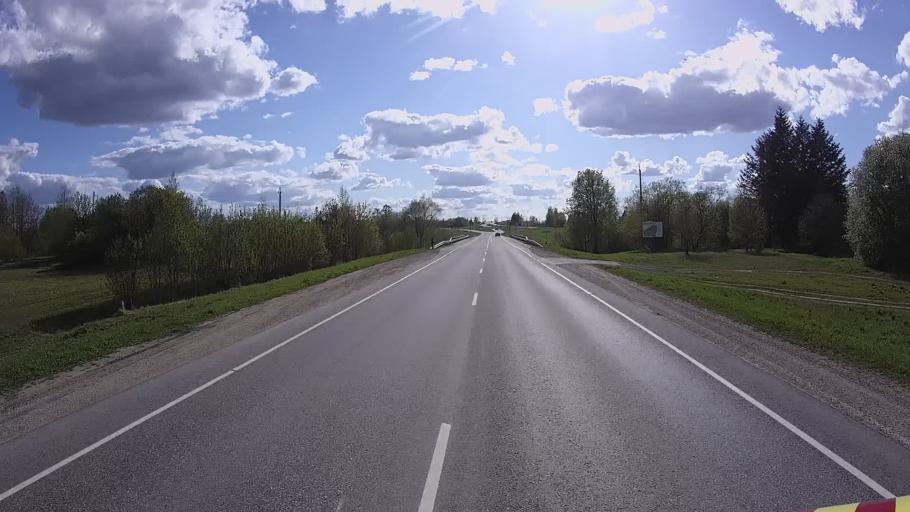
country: EE
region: Jogevamaa
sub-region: Jogeva linn
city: Jogeva
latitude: 58.7572
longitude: 26.4075
